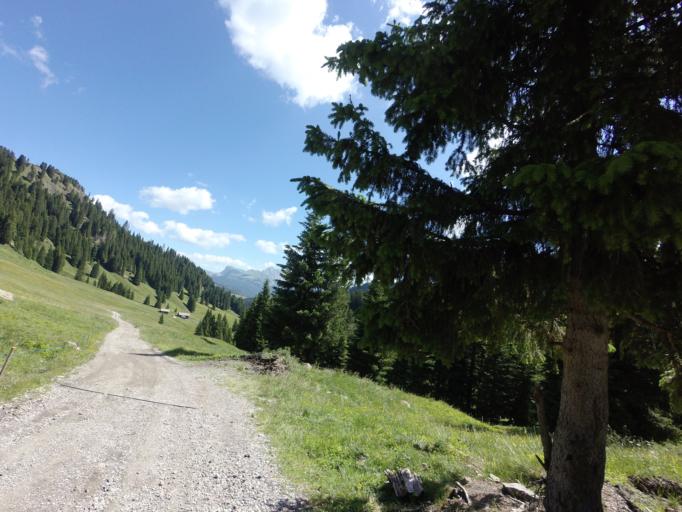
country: IT
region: Trentino-Alto Adige
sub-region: Provincia di Trento
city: Mazzin
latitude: 46.5085
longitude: 11.6585
